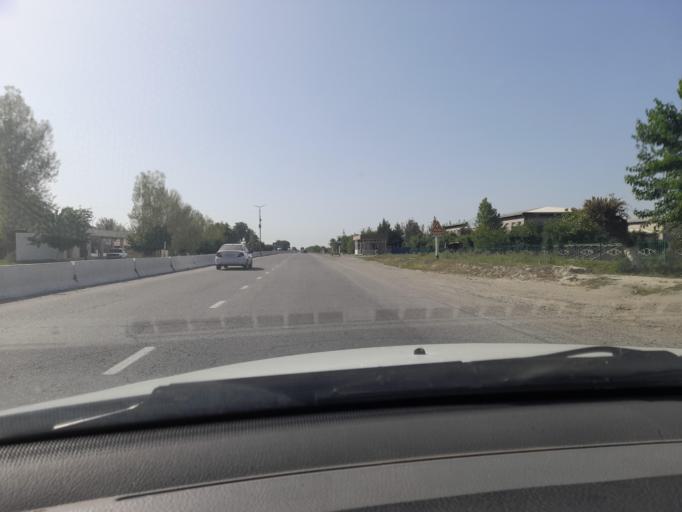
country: UZ
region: Samarqand
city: Chelak
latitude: 39.8398
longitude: 66.8204
